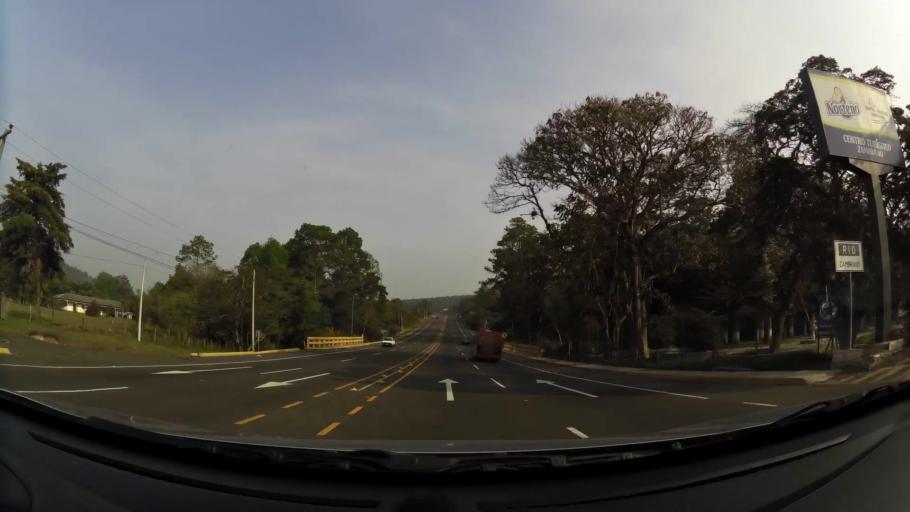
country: HN
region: Francisco Morazan
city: Zambrano
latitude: 14.2833
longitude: -87.4038
